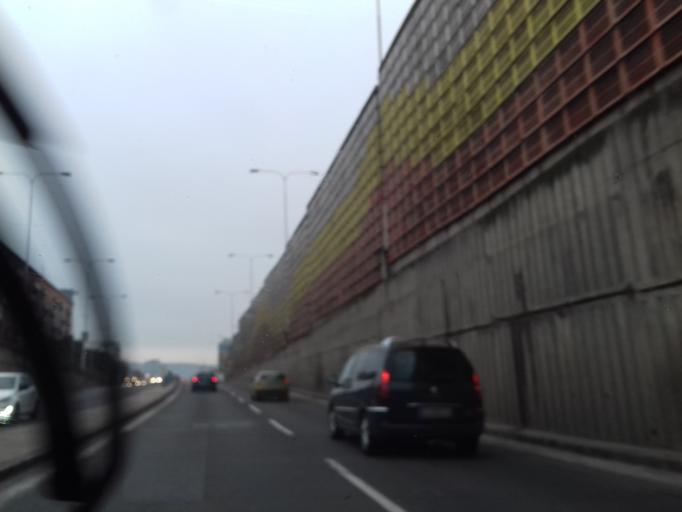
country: SK
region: Bratislavsky
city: Bratislava
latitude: 48.1492
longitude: 17.1497
